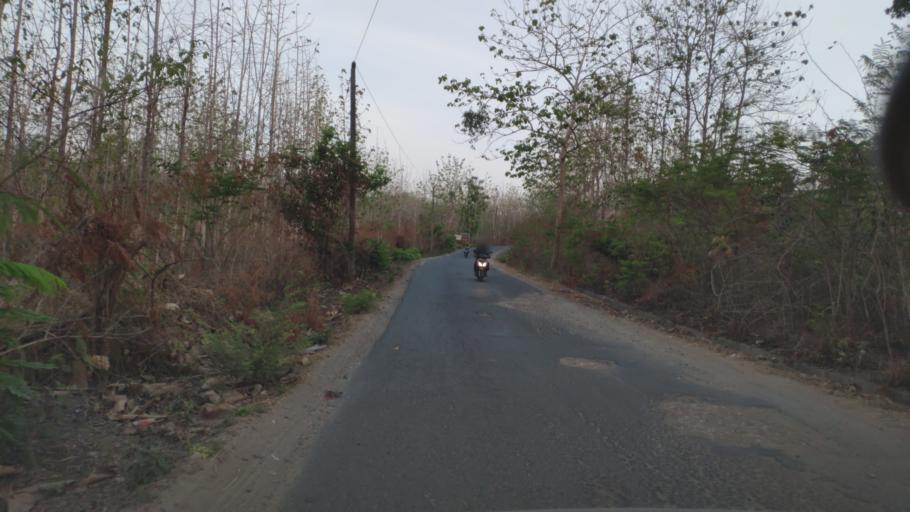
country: ID
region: Central Java
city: Semanggi
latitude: -7.0666
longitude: 111.4134
